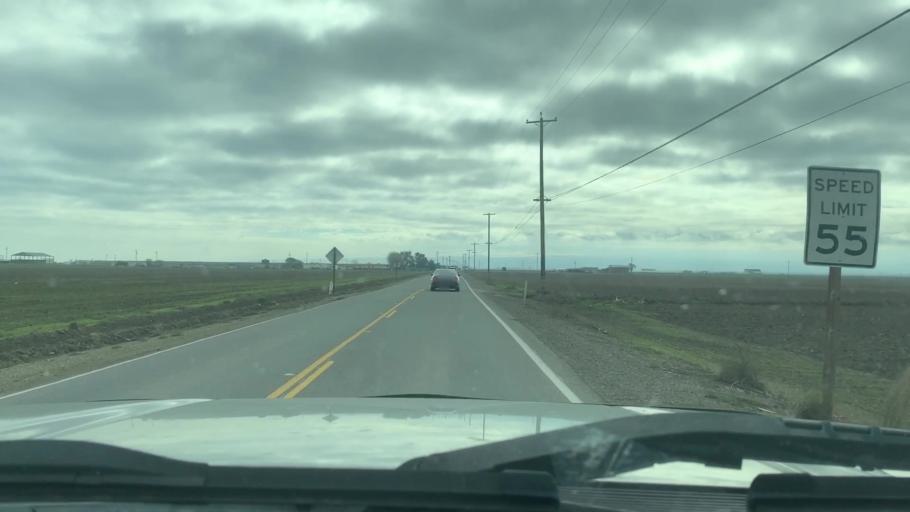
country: US
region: California
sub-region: Merced County
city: Los Banos
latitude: 37.0324
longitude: -120.8360
